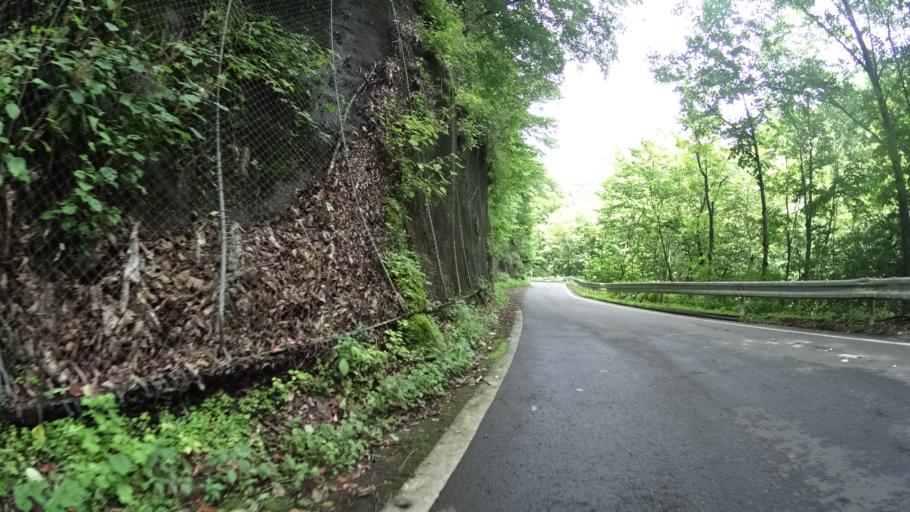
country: JP
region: Nagano
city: Saku
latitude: 36.0684
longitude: 138.6647
